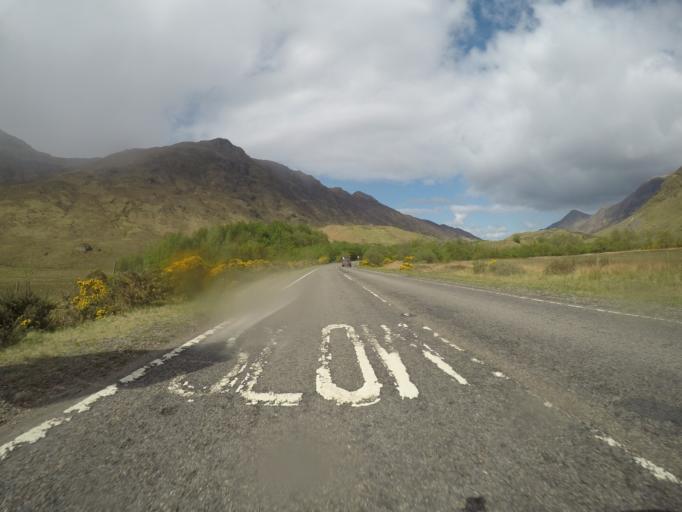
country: GB
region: Scotland
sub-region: Highland
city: Fort William
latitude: 57.1769
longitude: -5.3677
